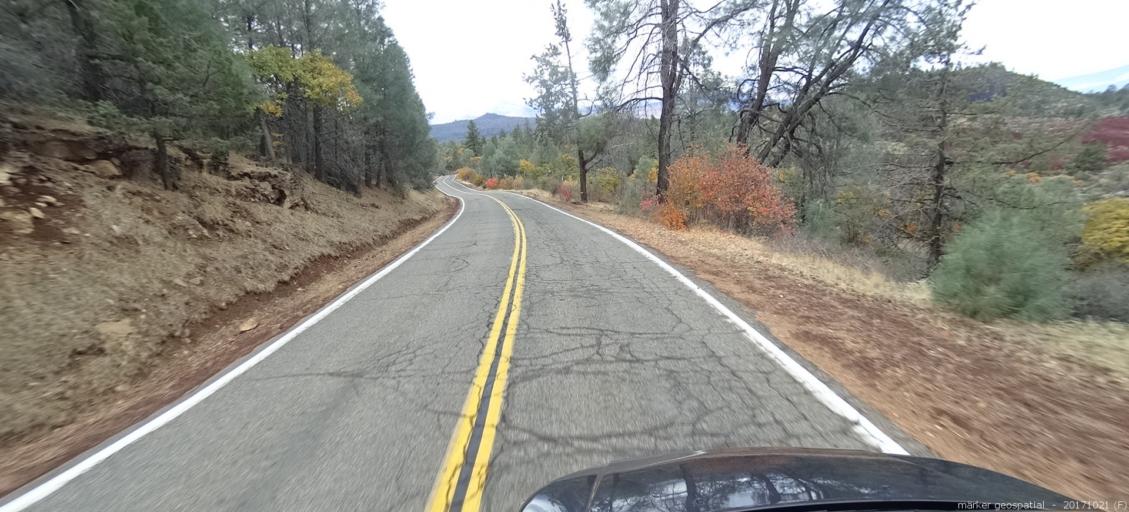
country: US
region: California
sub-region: Shasta County
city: Burney
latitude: 40.9261
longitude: -121.4560
